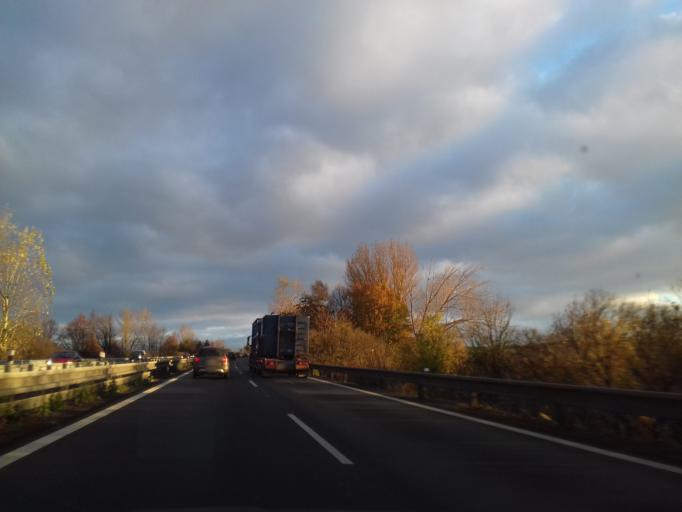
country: CZ
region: Olomoucky
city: Hnevotin
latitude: 49.5466
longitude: 17.1784
